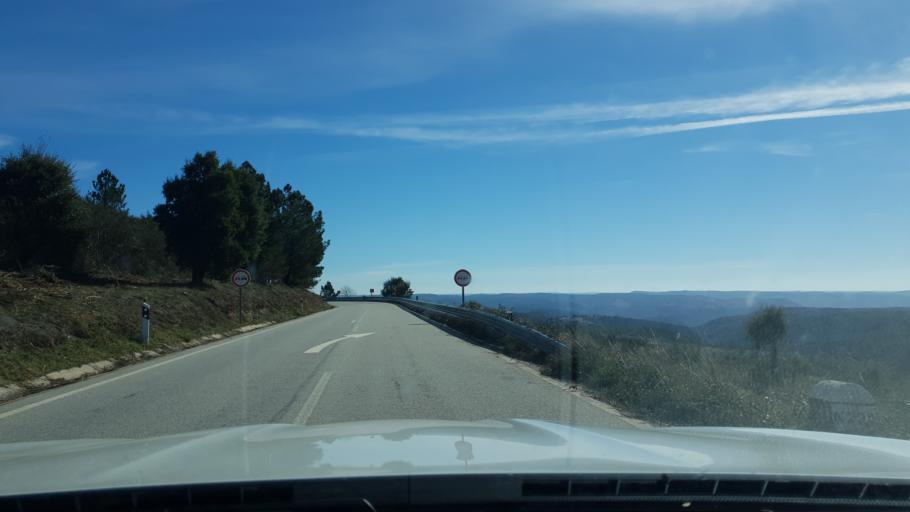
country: PT
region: Braganca
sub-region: Torre de Moncorvo
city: Torre de Moncorvo
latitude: 41.1795
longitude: -6.9293
